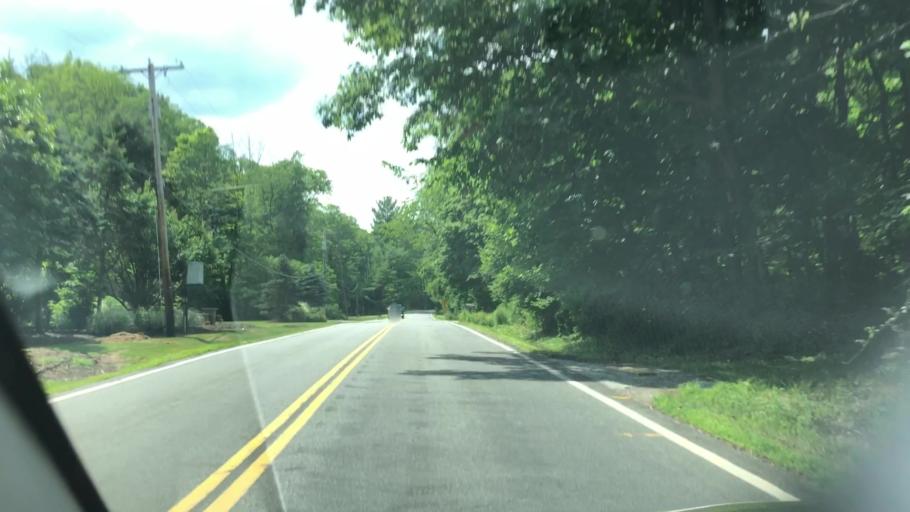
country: US
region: Ohio
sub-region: Summit County
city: Montrose-Ghent
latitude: 41.1595
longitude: -81.6442
